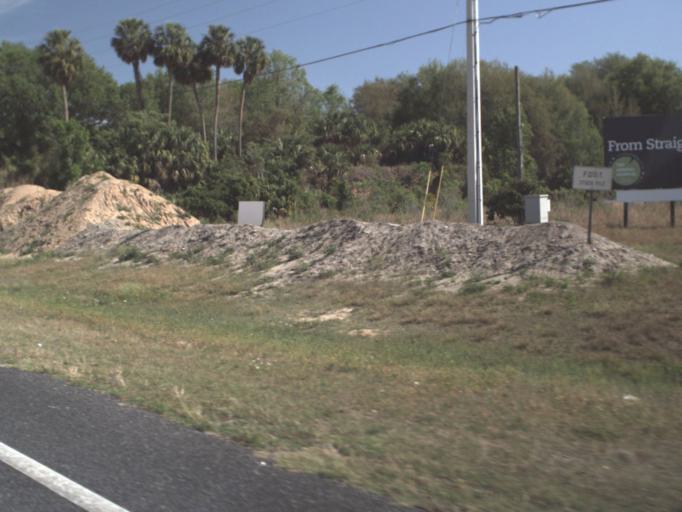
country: US
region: Florida
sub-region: Lake County
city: Hawthorne
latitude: 28.7771
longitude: -81.8873
